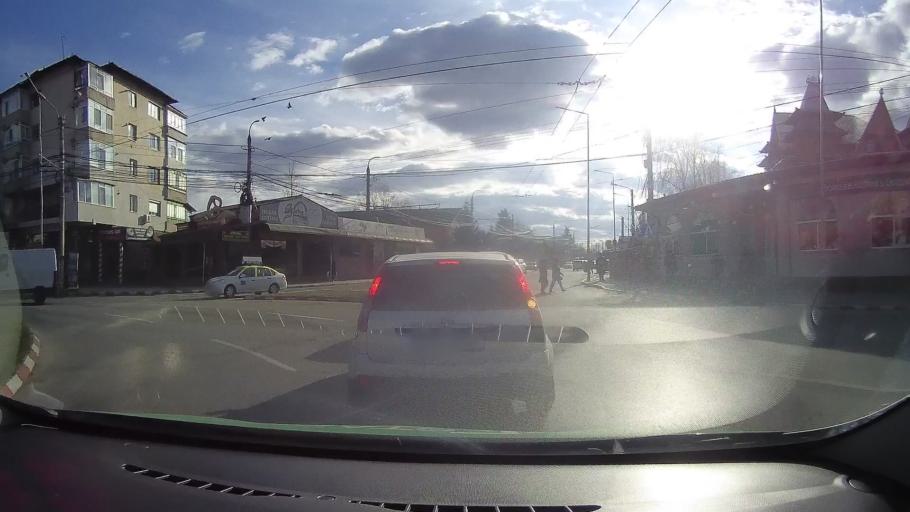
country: RO
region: Dambovita
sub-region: Comuna Lucieni
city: Lucieni
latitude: 44.8583
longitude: 25.4196
